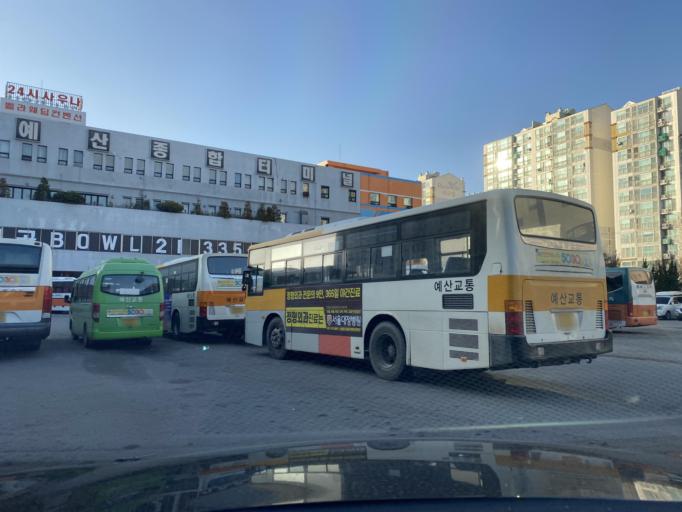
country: KR
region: Chungcheongnam-do
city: Yesan
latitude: 36.6942
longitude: 126.8332
